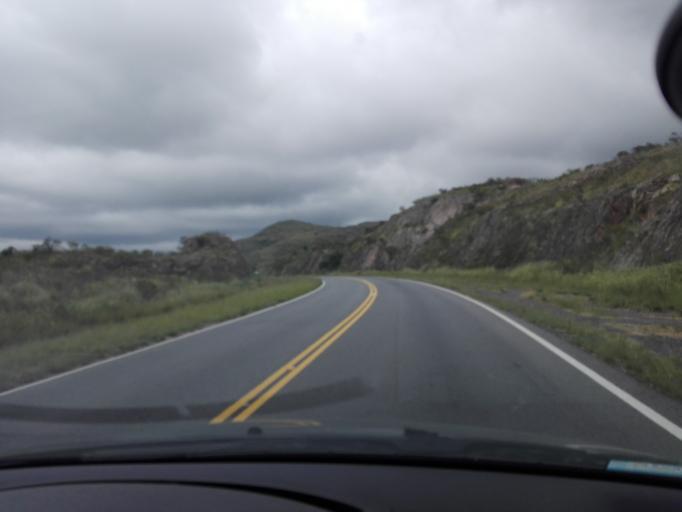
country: AR
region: Cordoba
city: Cuesta Blanca
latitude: -31.5934
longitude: -64.6789
